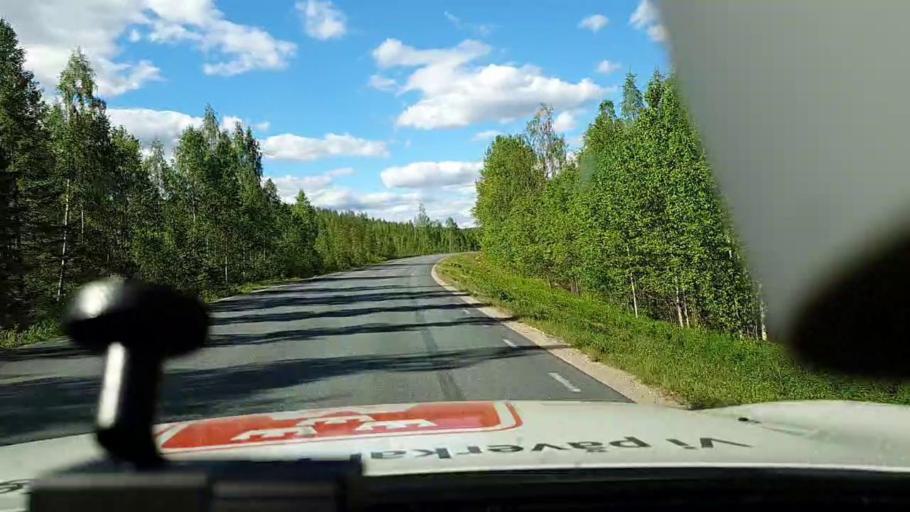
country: FI
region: Lapland
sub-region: Torniolaakso
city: Ylitornio
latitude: 66.3137
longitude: 23.6199
